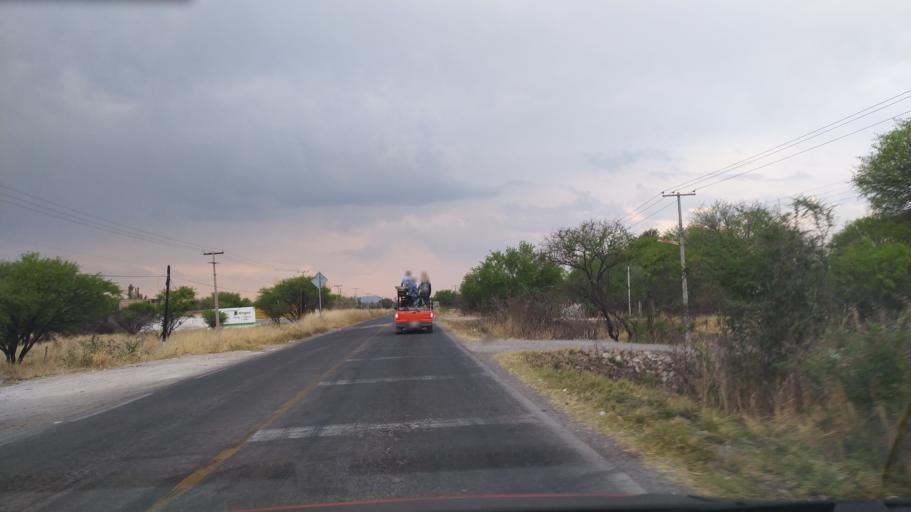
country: MX
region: Guanajuato
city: Ciudad Manuel Doblado
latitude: 20.7982
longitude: -101.9057
